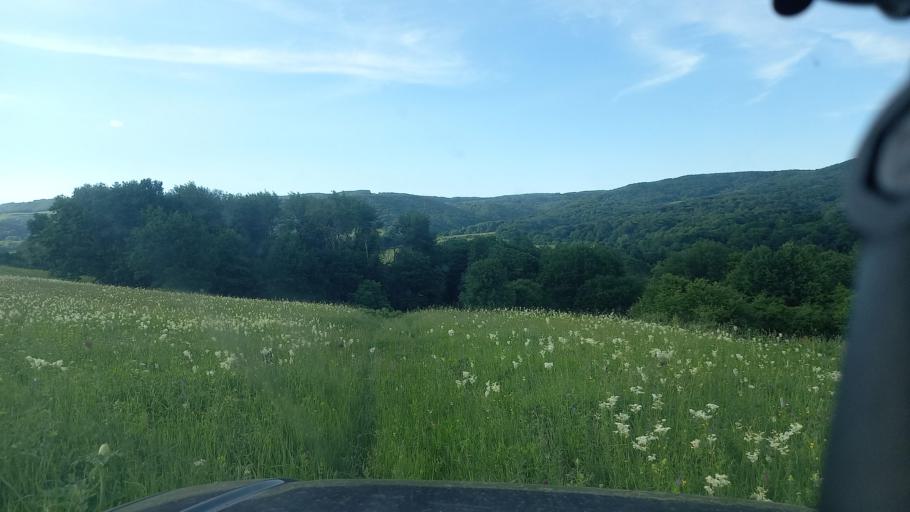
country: RU
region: Karachayevo-Cherkesiya
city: Kurdzhinovo
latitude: 44.1324
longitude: 41.0954
